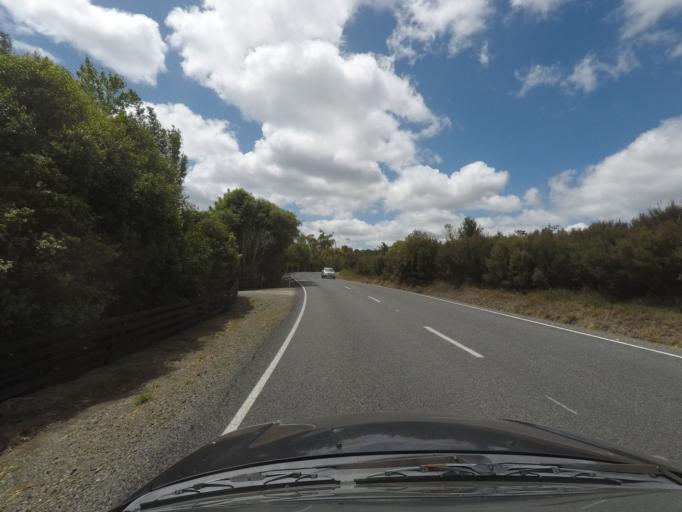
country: NZ
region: Northland
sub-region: Whangarei
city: Ruakaka
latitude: -36.0189
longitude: 174.4921
